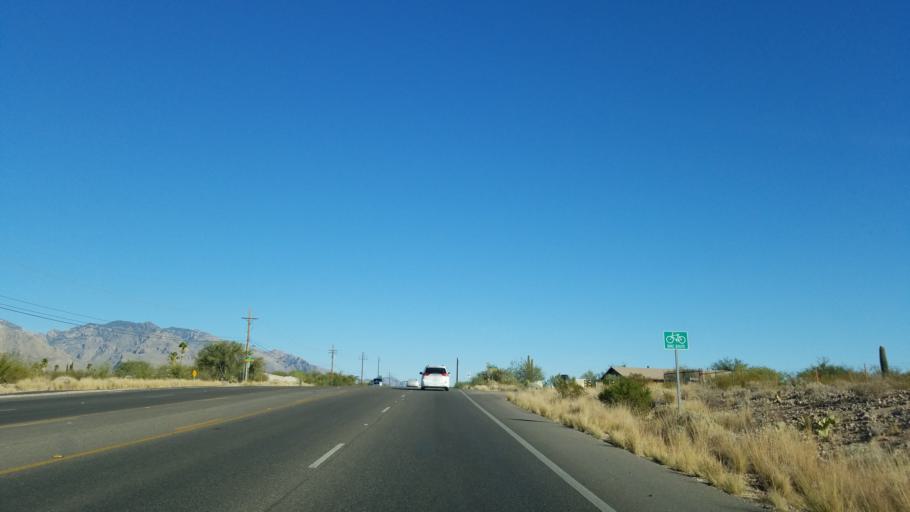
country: US
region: Arizona
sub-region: Pima County
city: Casas Adobes
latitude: 32.3231
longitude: -111.0247
